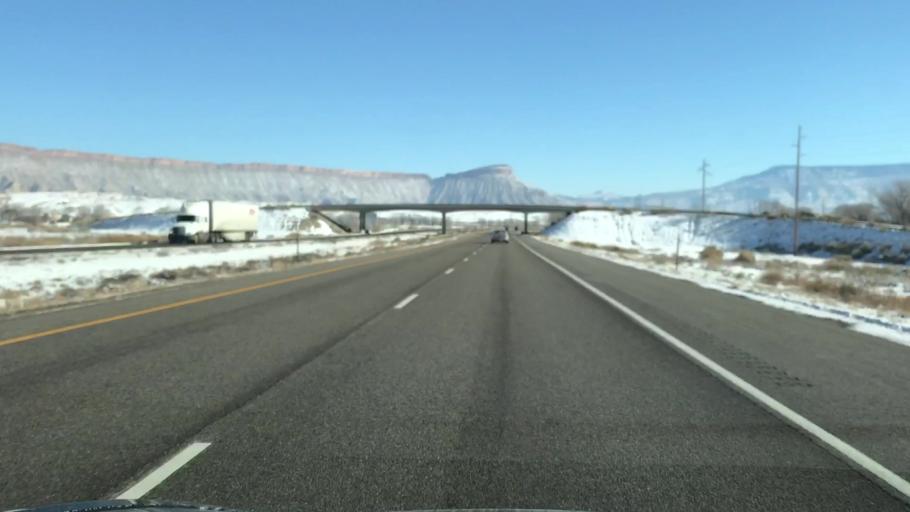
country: US
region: Colorado
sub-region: Mesa County
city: Fruitvale
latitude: 39.1077
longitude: -108.5134
